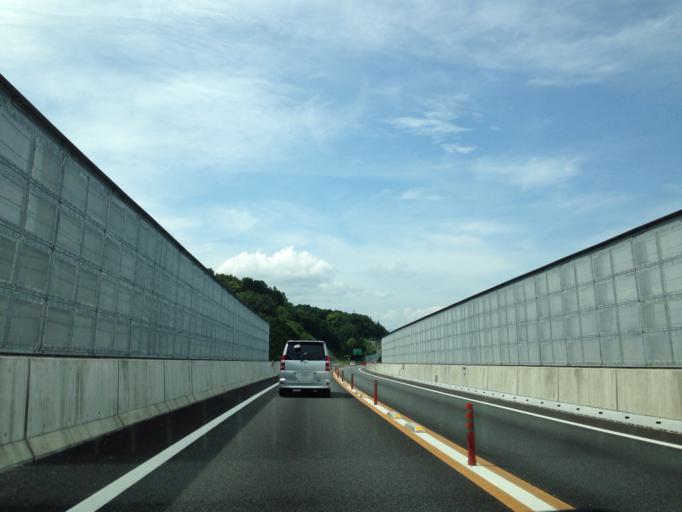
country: JP
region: Shizuoka
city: Mishima
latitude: 35.1175
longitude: 138.9497
